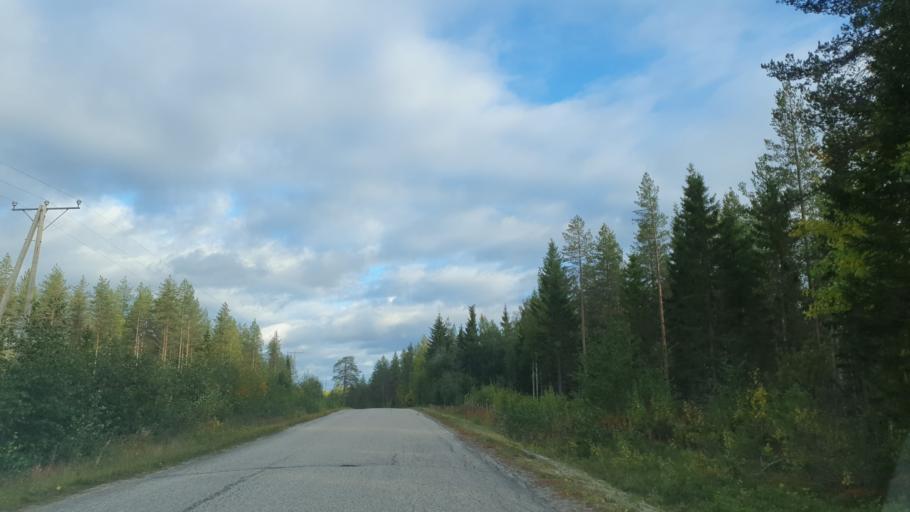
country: FI
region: Kainuu
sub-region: Kehys-Kainuu
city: Kuhmo
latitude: 63.9228
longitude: 30.0433
